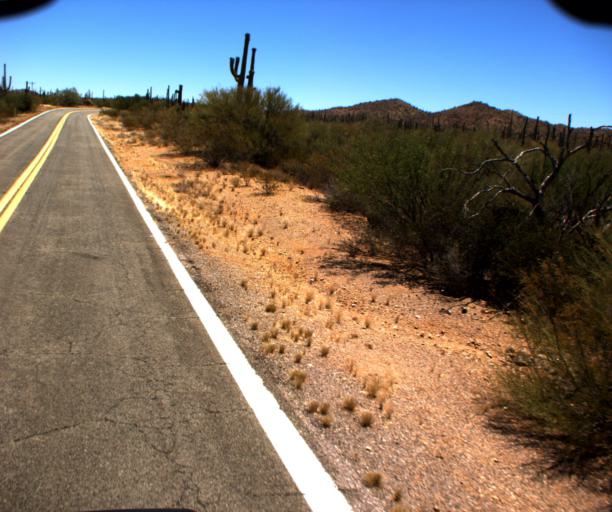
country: US
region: Arizona
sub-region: Pima County
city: Sells
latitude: 32.1730
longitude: -112.2044
